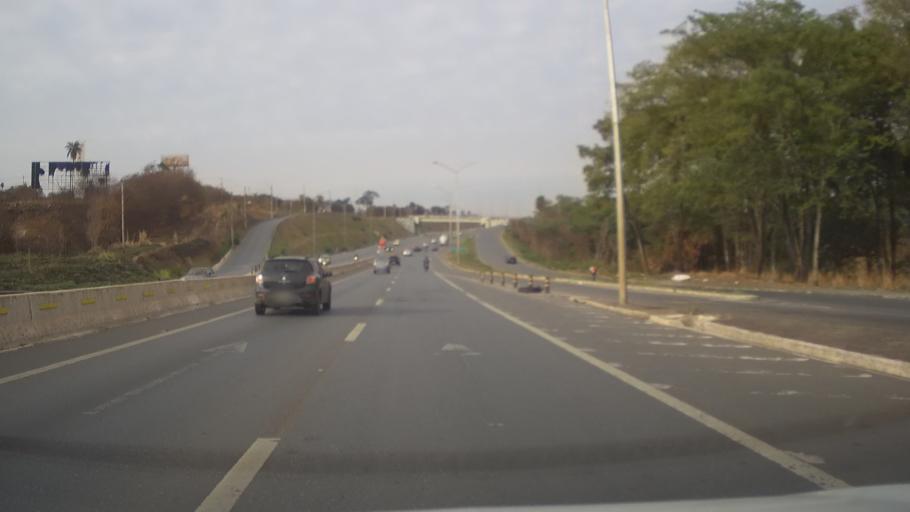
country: BR
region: Minas Gerais
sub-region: Vespasiano
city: Vespasiano
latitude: -19.7191
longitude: -43.9306
